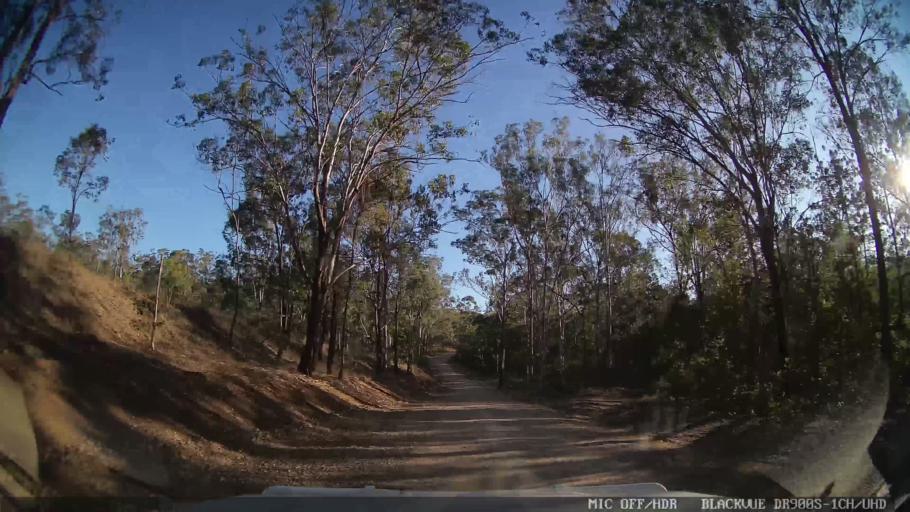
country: AU
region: Queensland
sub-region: Gladstone
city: Toolooa
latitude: -24.6834
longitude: 151.3306
